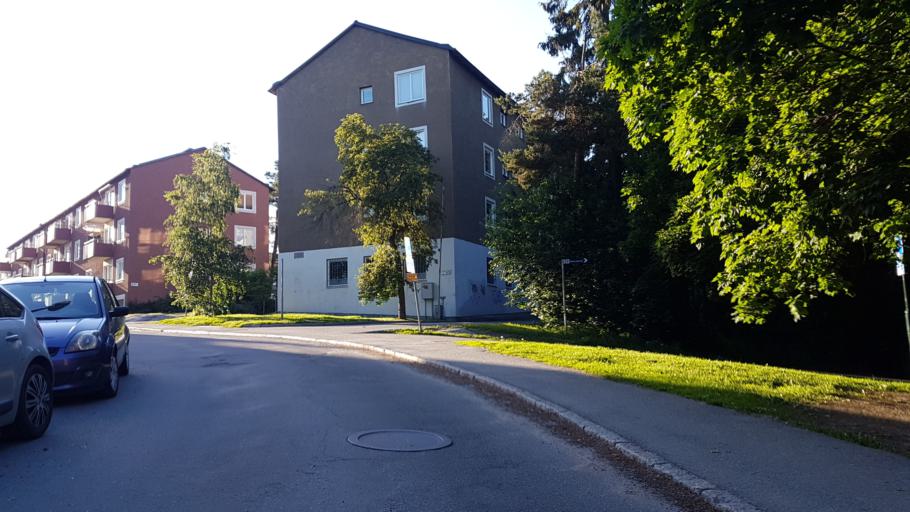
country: SE
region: Stockholm
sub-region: Nacka Kommun
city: Nacka
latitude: 59.2841
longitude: 18.1199
